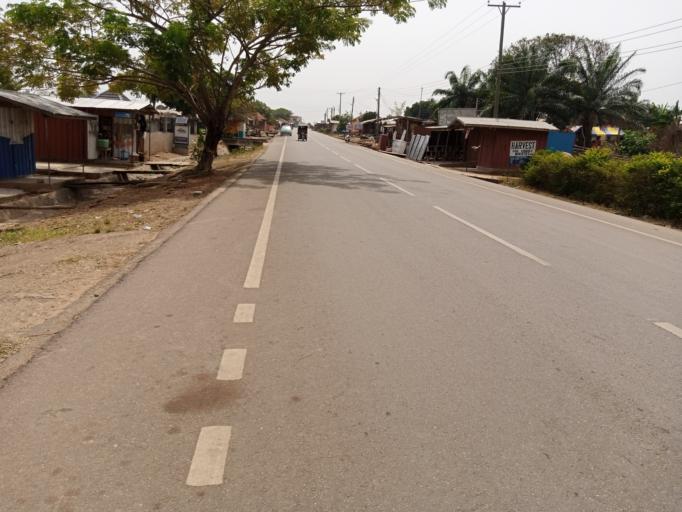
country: GH
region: Volta
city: Kpandu
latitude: 7.0060
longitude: 0.2957
